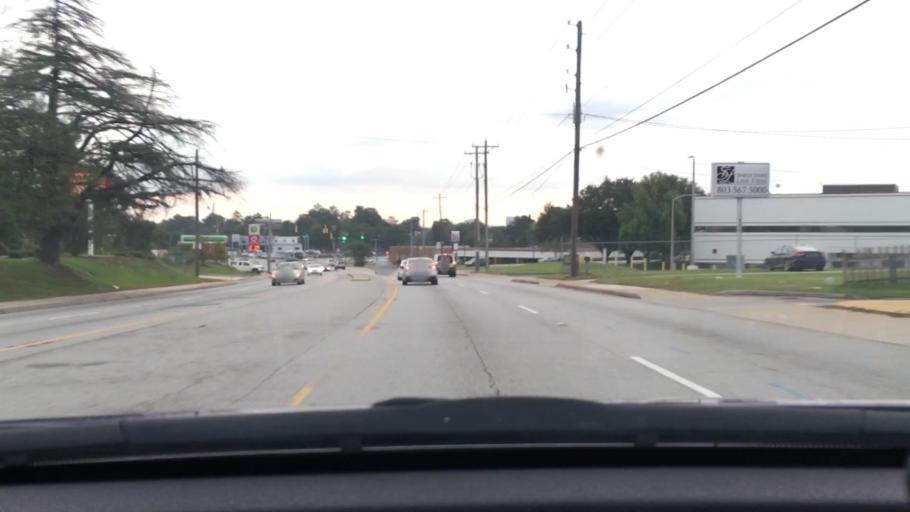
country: US
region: South Carolina
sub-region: Lexington County
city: West Columbia
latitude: 34.0254
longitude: -81.0805
